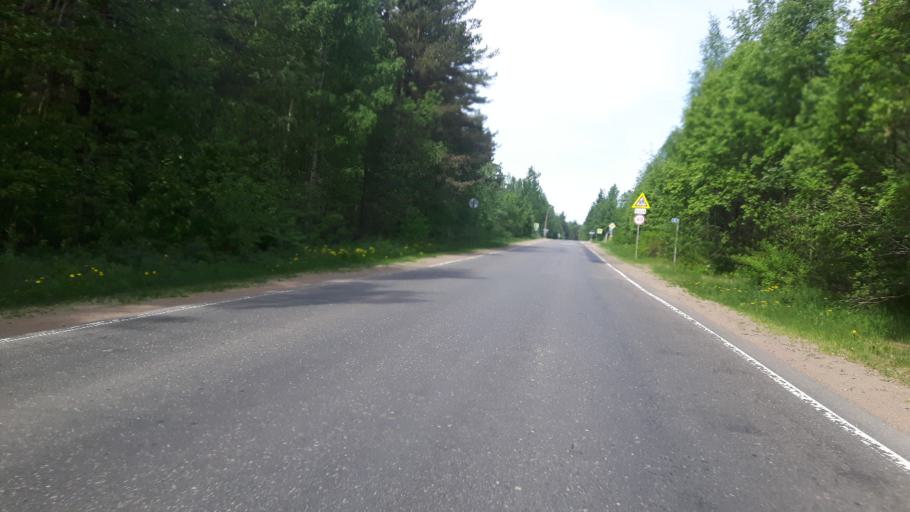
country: RU
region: Leningrad
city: Ust'-Luga
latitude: 59.6443
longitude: 28.2706
